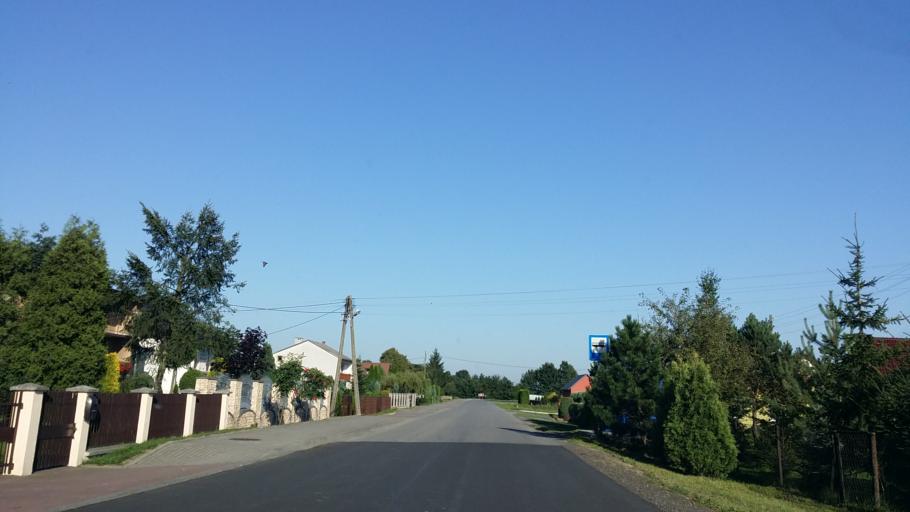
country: PL
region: Lesser Poland Voivodeship
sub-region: Powiat wadowicki
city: Spytkowice
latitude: 50.0156
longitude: 19.5095
